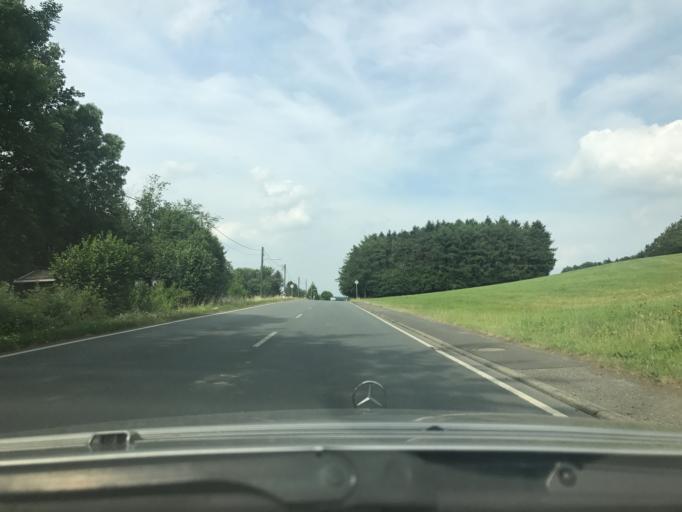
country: DE
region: North Rhine-Westphalia
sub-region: Regierungsbezirk Arnsberg
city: Holzwickede
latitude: 51.4543
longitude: 7.6869
